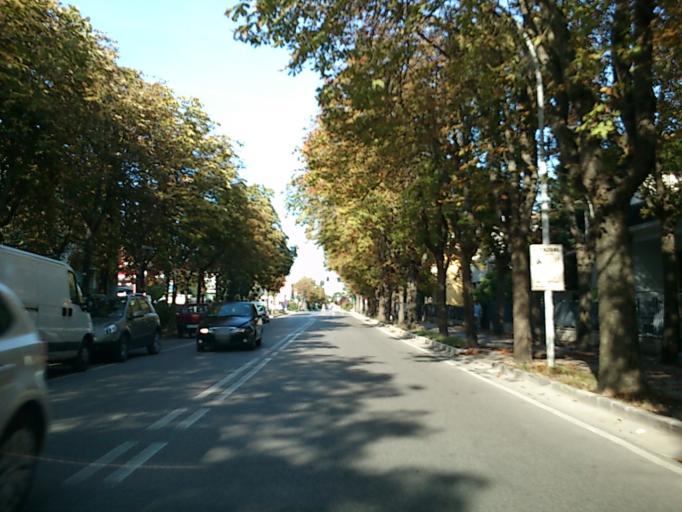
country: IT
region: The Marches
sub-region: Provincia di Pesaro e Urbino
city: Fossombrone
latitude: 43.6908
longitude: 12.8135
